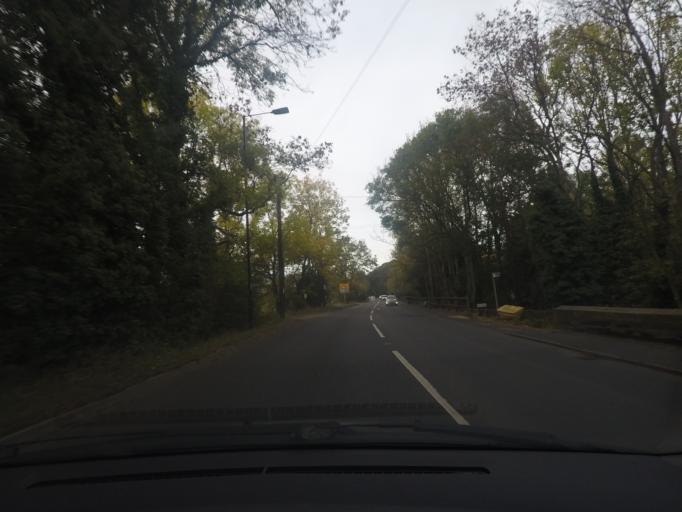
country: GB
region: England
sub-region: Sheffield
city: Chapletown
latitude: 53.4538
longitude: -1.4942
